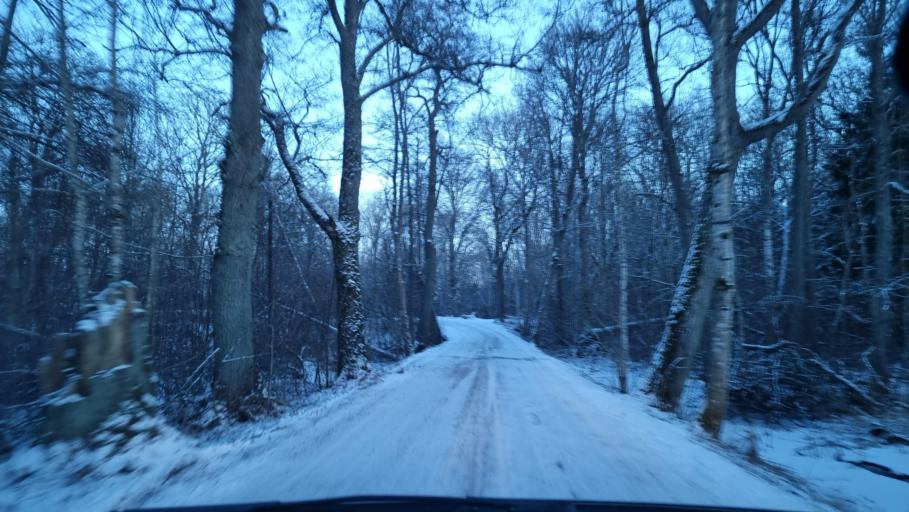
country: SE
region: Stockholm
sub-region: Vallentuna Kommun
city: Vallentuna
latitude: 59.5828
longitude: 18.1151
